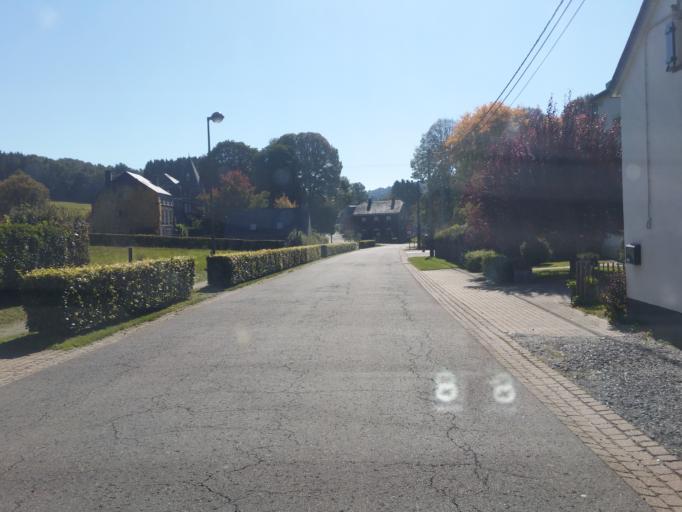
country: BE
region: Wallonia
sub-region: Province du Luxembourg
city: Herbeumont
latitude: 49.7789
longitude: 5.2392
